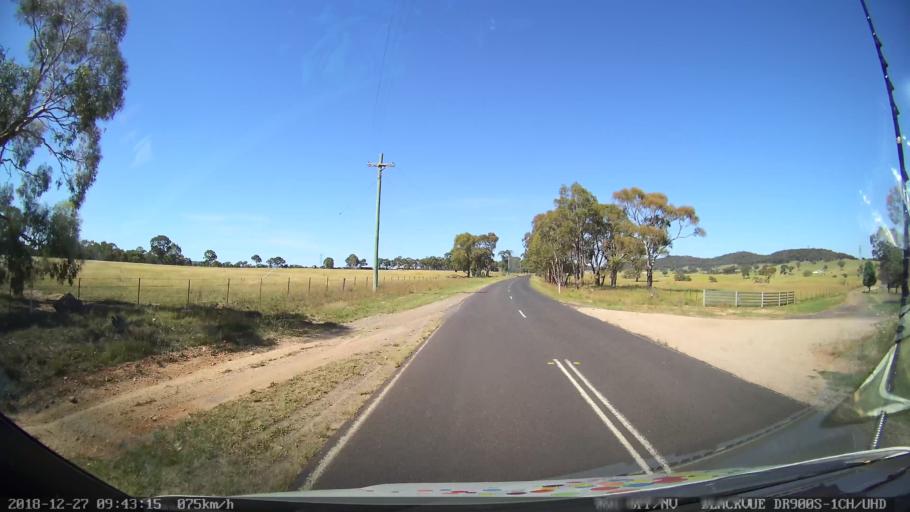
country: AU
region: New South Wales
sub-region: Lithgow
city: Portland
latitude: -33.3047
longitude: 150.0029
